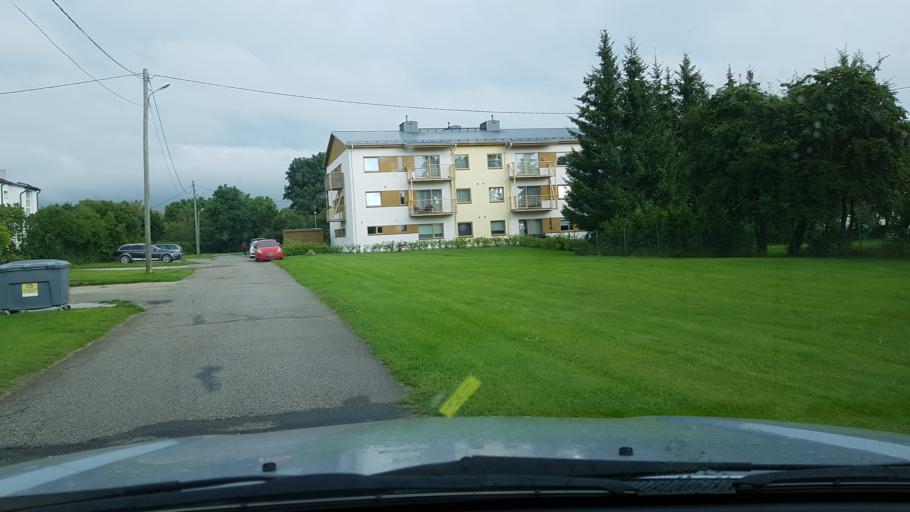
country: EE
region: Harju
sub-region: Joelaehtme vald
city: Loo
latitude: 59.4018
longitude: 24.9326
